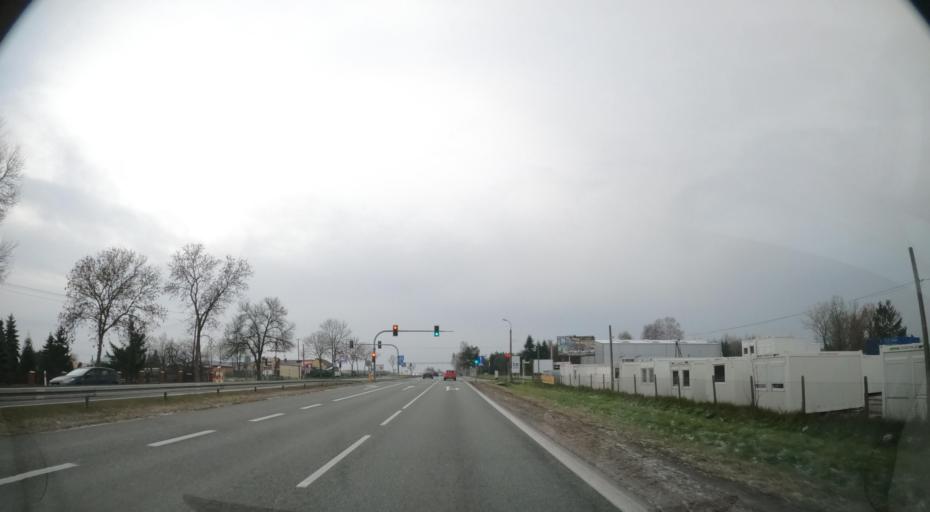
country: PL
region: Masovian Voivodeship
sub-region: Powiat piaseczynski
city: Tarczyn
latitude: 52.0100
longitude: 20.8480
